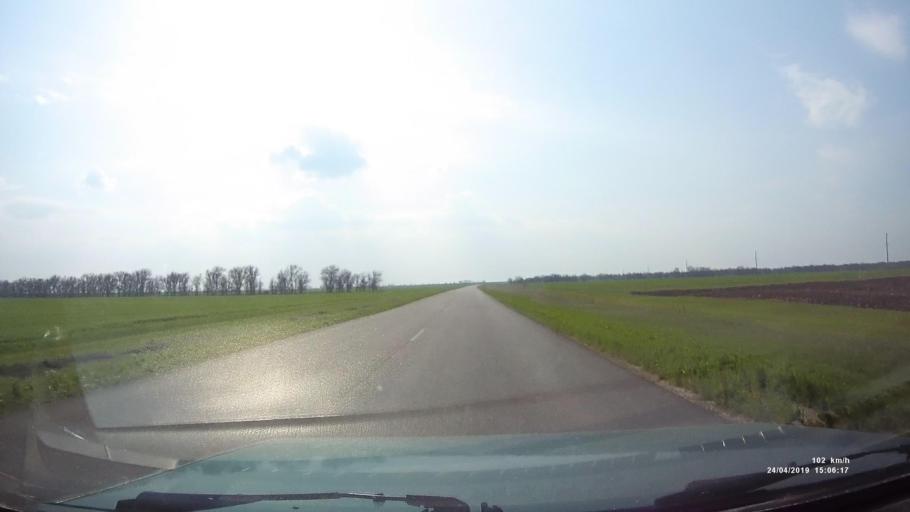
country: RU
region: Rostov
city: Remontnoye
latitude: 46.5590
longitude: 43.4308
